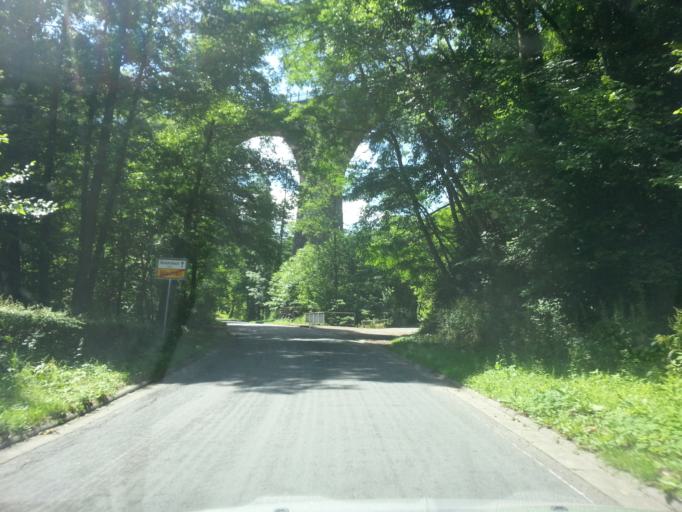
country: DE
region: Hesse
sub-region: Regierungsbezirk Darmstadt
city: Morlenbach
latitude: 49.5798
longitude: 8.7691
